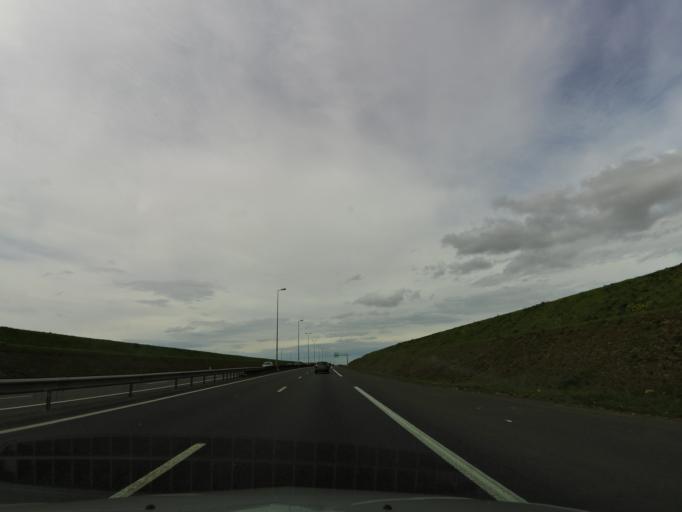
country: FR
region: Lower Normandy
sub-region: Departement du Calvados
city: Eterville
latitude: 49.1471
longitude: -0.4106
